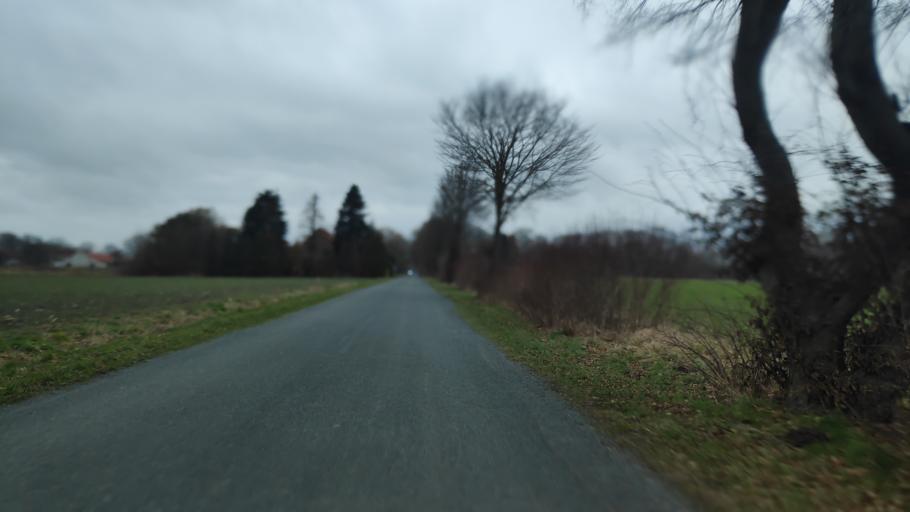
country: DE
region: North Rhine-Westphalia
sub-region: Regierungsbezirk Detmold
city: Hille
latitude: 52.3738
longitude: 8.7740
